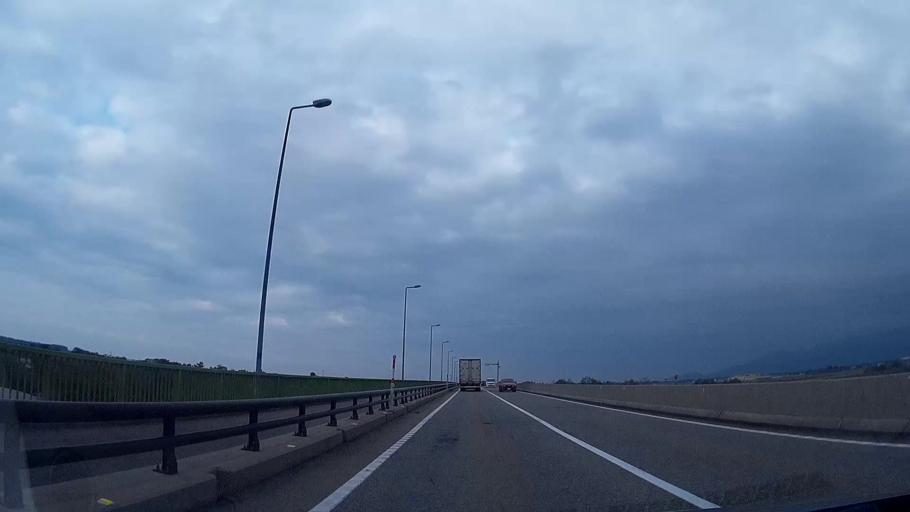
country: JP
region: Toyama
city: Nyuzen
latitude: 36.9035
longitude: 137.4492
